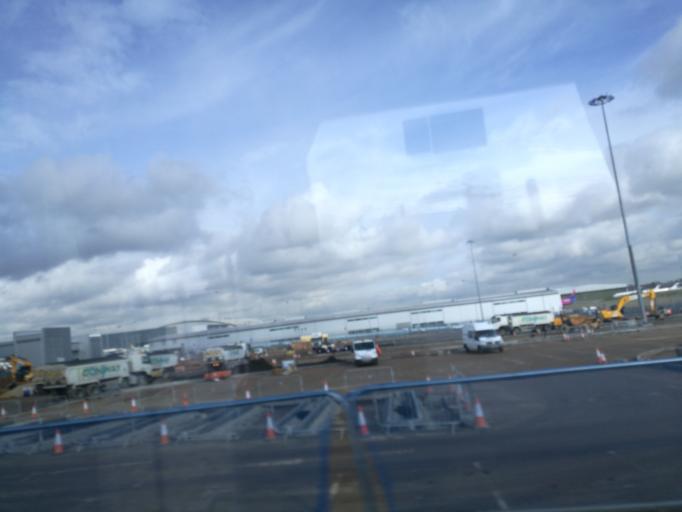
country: GB
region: England
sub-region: Luton
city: Luton
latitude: 51.8772
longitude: -0.3714
